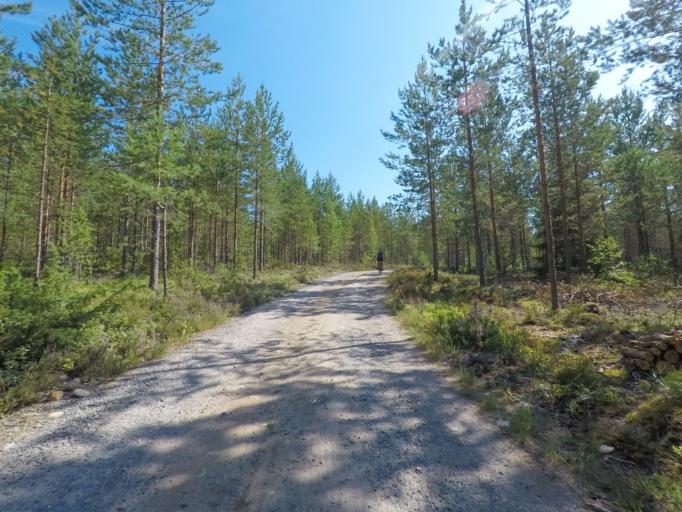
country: FI
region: Southern Savonia
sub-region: Mikkeli
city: Puumala
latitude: 61.4294
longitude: 28.0062
